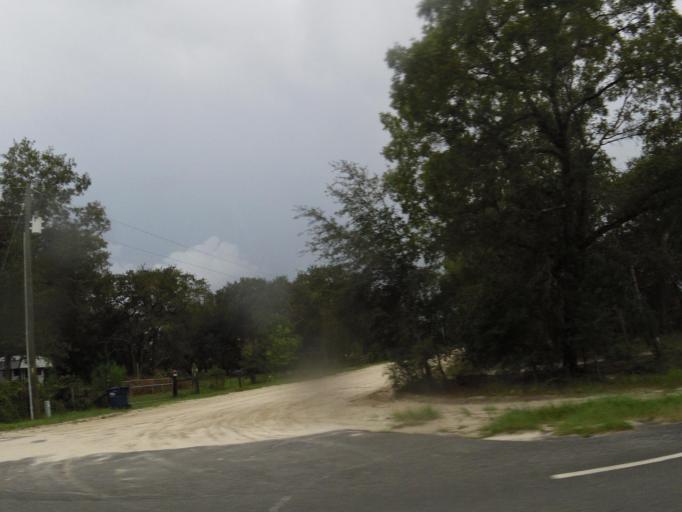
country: US
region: Florida
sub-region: Baker County
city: Macclenny
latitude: 30.4123
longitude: -82.1942
